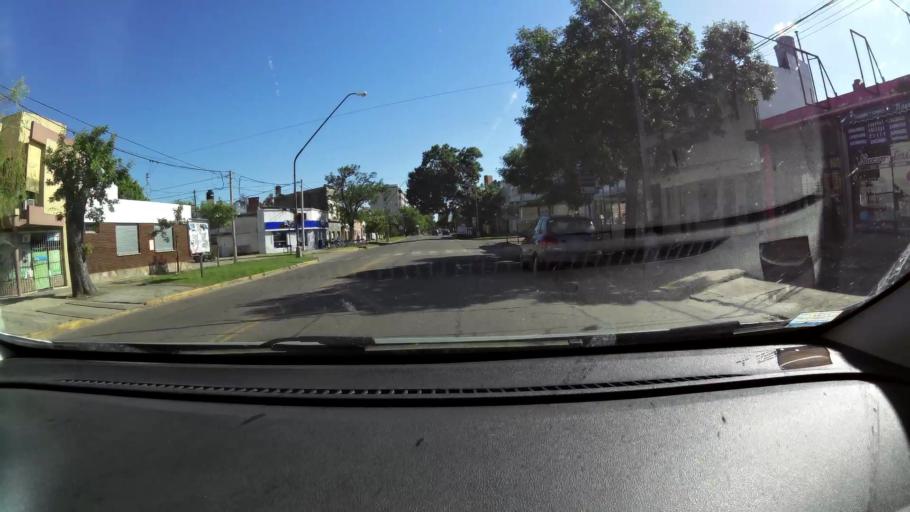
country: AR
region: Santa Fe
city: Santa Fe de la Vera Cruz
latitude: -31.6280
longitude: -60.6912
